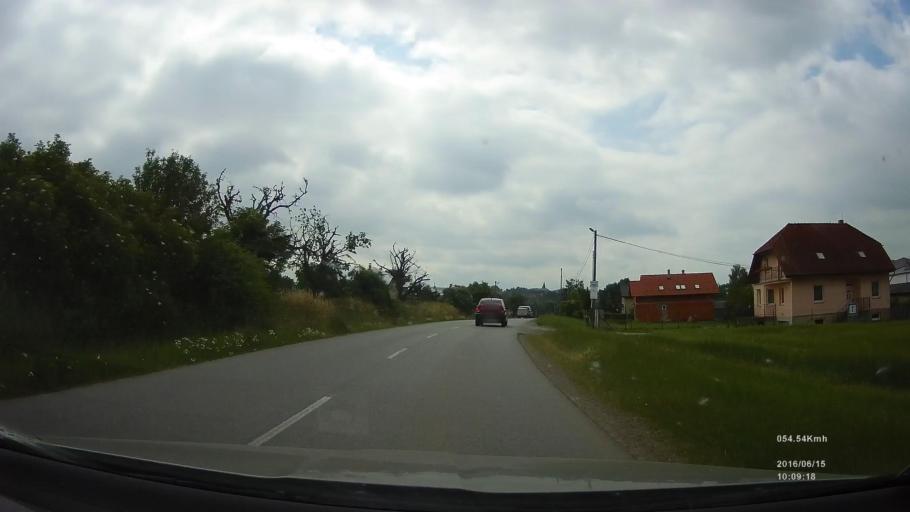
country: SK
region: Kosicky
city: Kosice
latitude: 48.7600
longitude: 21.3390
